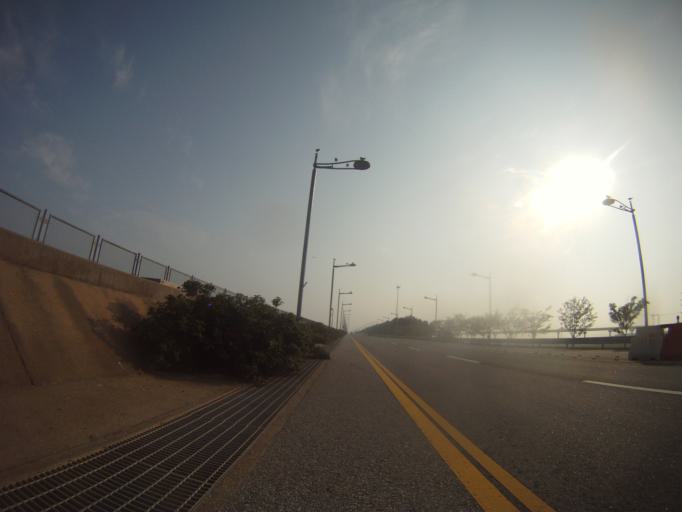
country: KR
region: Incheon
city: Incheon
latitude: 37.4307
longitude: 126.4590
